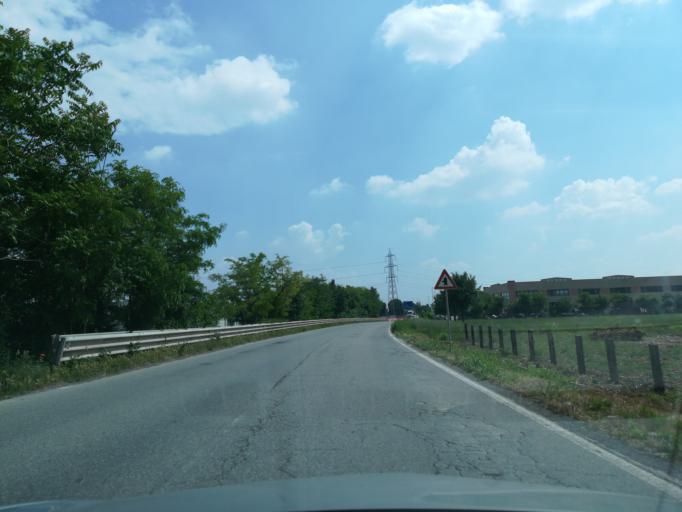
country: IT
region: Lombardy
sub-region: Provincia di Bergamo
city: Costa di Mezzate
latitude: 45.6511
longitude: 9.8082
